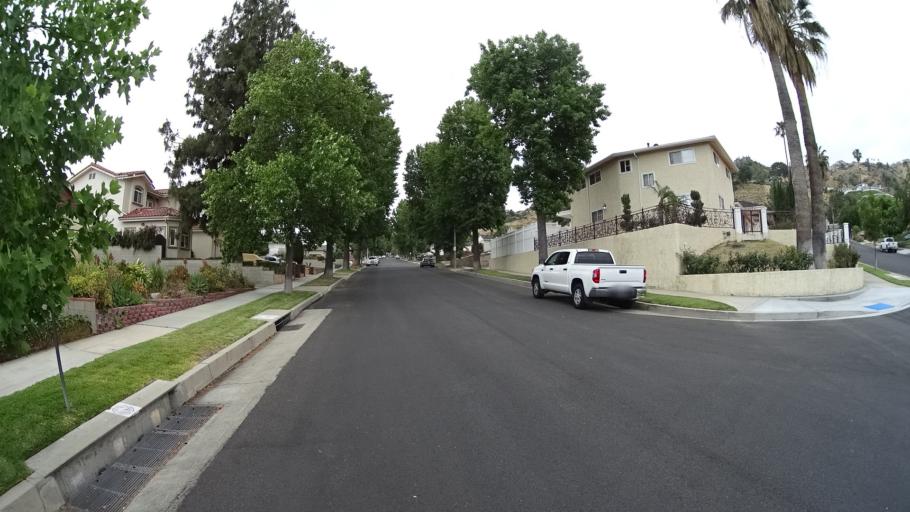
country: US
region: California
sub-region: Los Angeles County
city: Burbank
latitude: 34.2048
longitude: -118.3269
